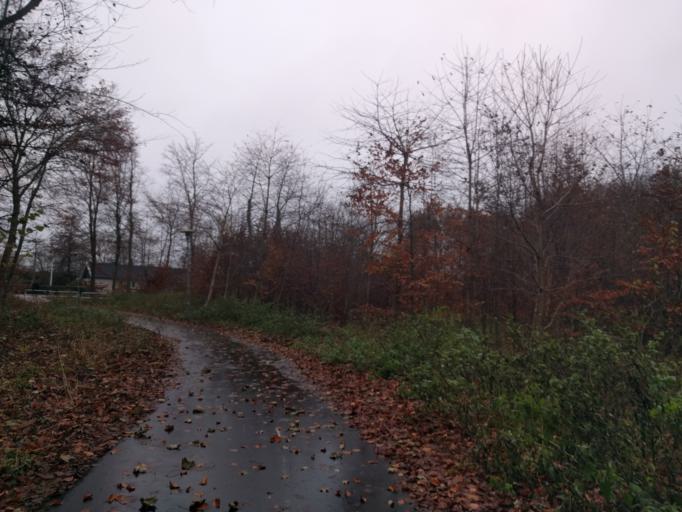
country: DK
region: South Denmark
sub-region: Fredericia Kommune
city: Snoghoj
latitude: 55.5408
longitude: 9.7194
